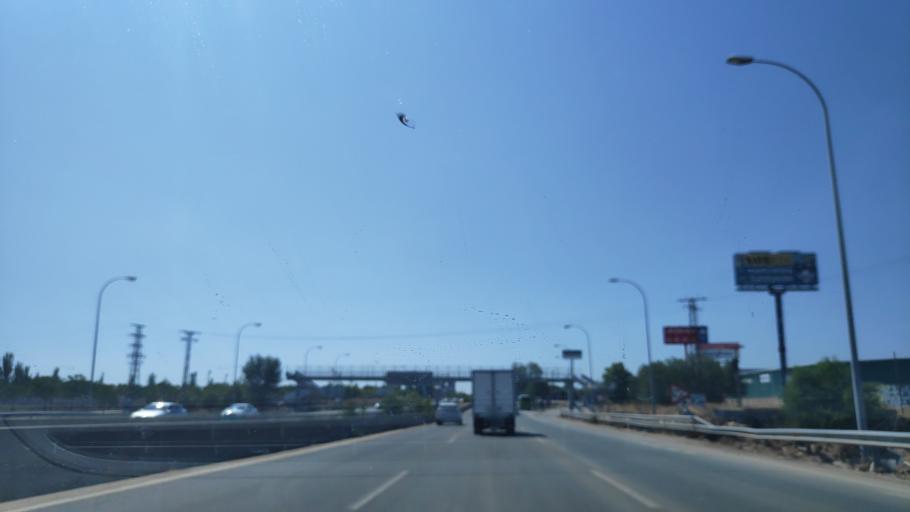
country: ES
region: Madrid
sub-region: Provincia de Madrid
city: Villaverde
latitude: 40.3528
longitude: -3.7224
